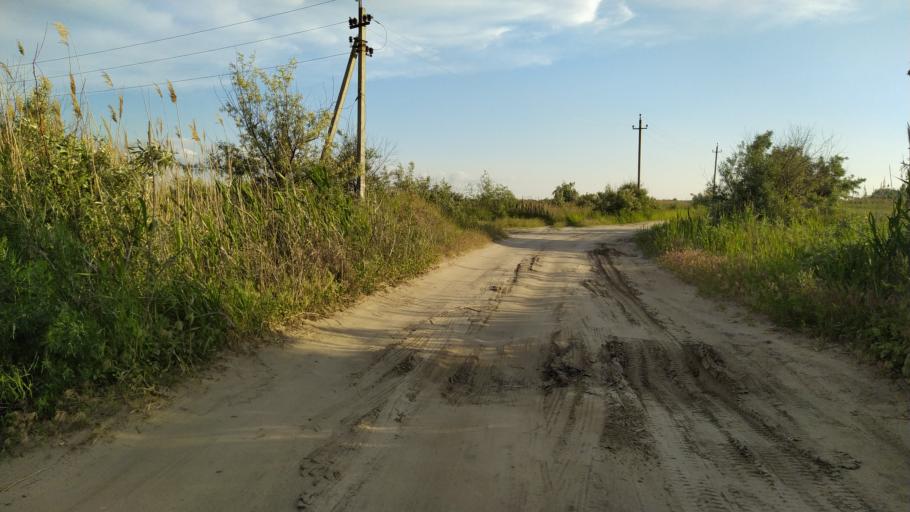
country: RU
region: Rostov
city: Bataysk
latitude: 47.1429
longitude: 39.6676
